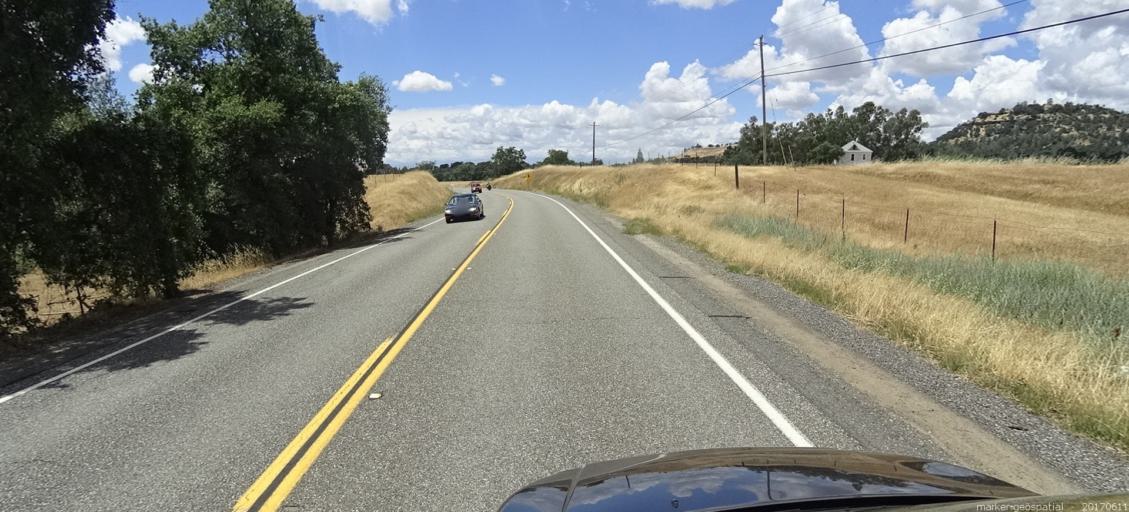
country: US
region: California
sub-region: Butte County
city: Paradise
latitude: 39.6555
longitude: -121.5815
